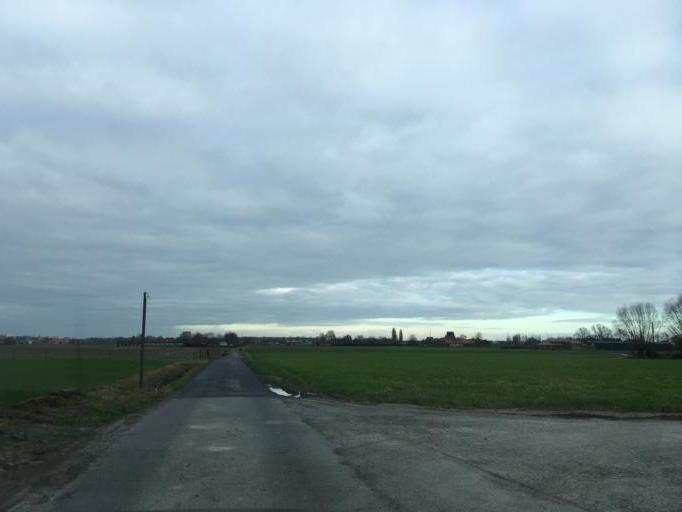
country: BE
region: Flanders
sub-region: Provincie West-Vlaanderen
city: Ledegem
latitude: 50.8932
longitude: 3.1390
